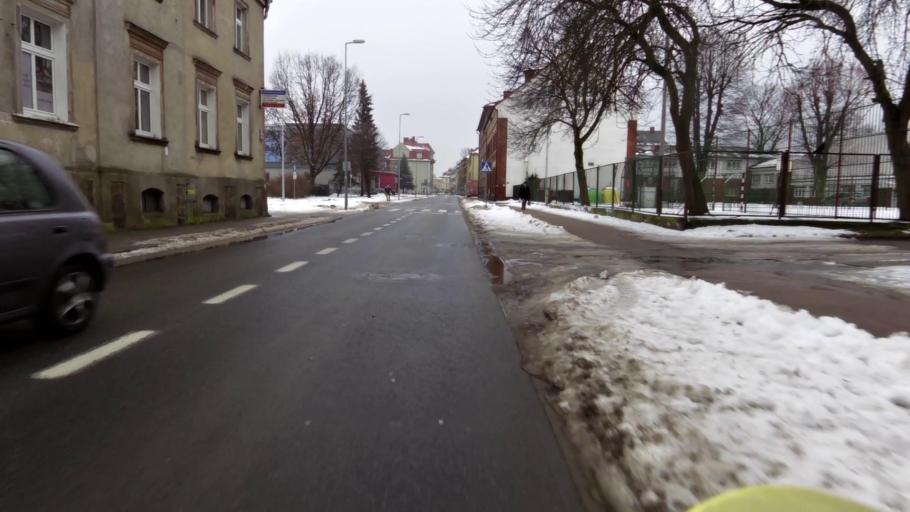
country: PL
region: West Pomeranian Voivodeship
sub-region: Powiat szczecinecki
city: Szczecinek
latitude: 53.7124
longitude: 16.6926
